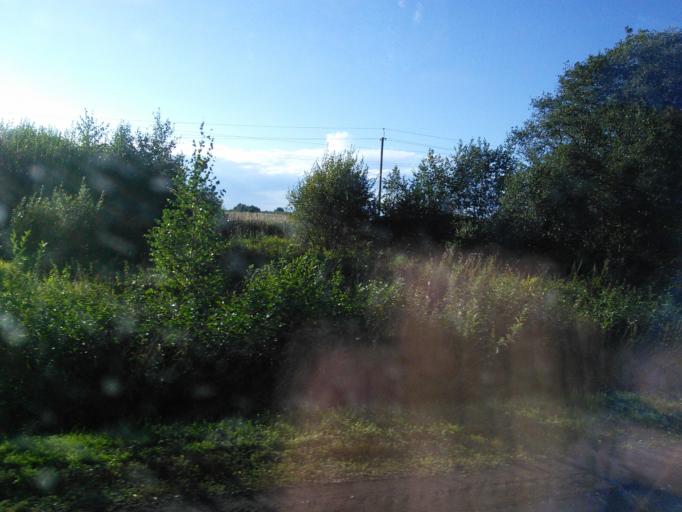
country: RU
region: Jaroslavl
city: Poshekhon'ye
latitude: 58.4596
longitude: 39.0409
